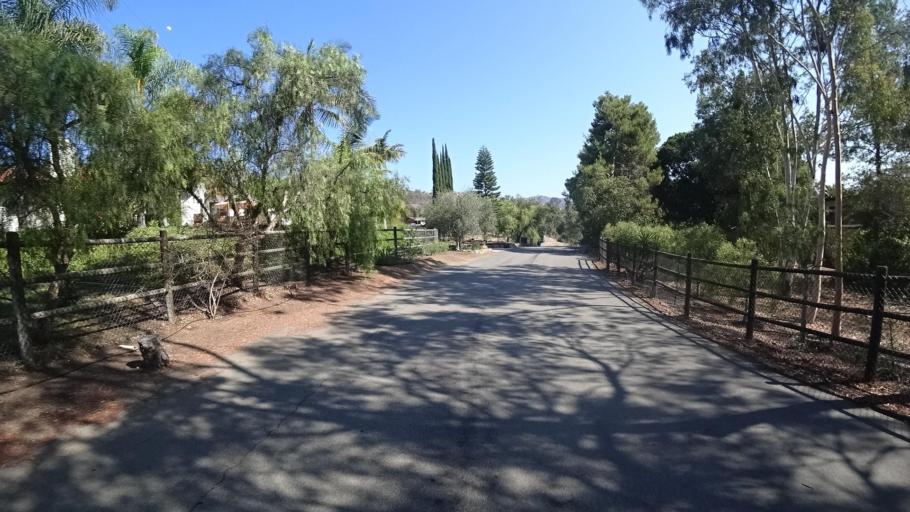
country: US
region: California
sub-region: San Diego County
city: Rancho Santa Fe
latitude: 33.0329
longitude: -117.1686
